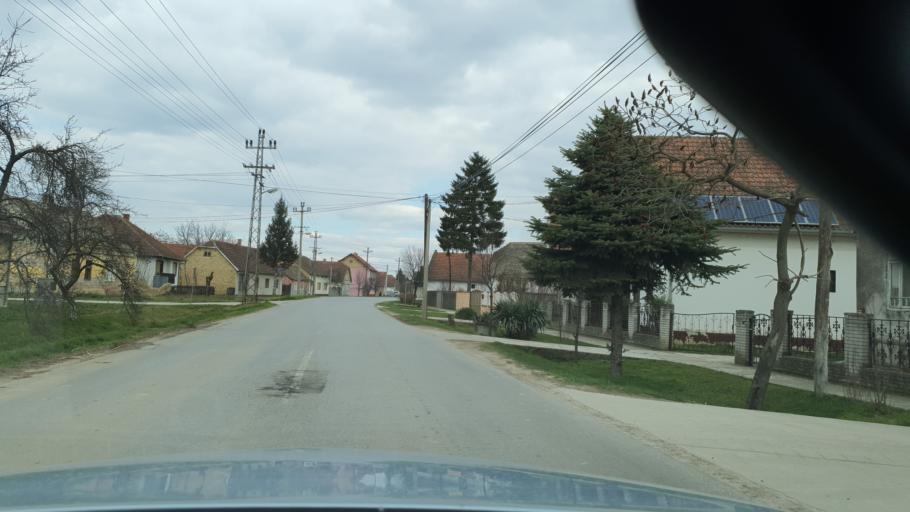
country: RS
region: Autonomna Pokrajina Vojvodina
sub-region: Juznobacki Okrug
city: Bac
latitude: 45.4058
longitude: 19.2911
